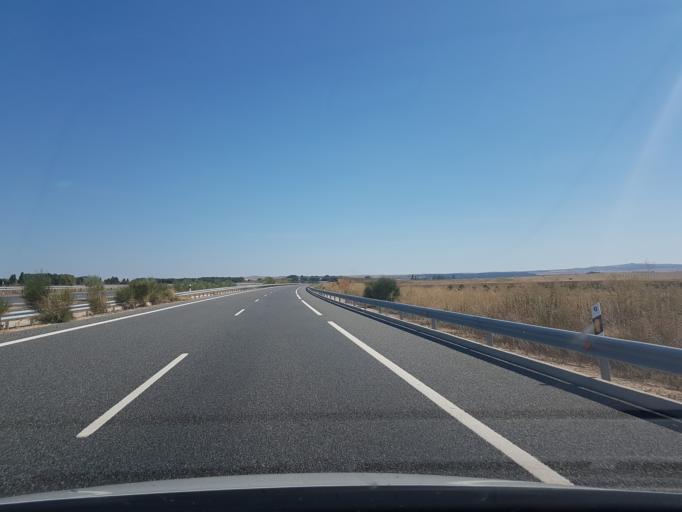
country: ES
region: Castille and Leon
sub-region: Provincia de Avila
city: Munogrande
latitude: 40.8134
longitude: -4.9090
